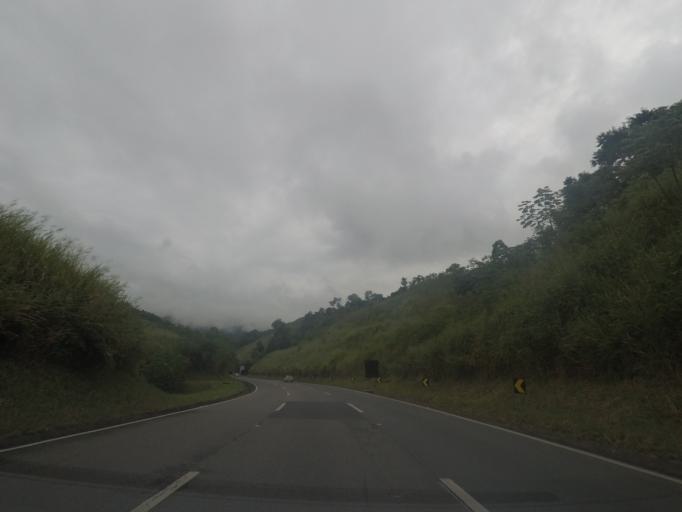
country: BR
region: Sao Paulo
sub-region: Cajati
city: Cajati
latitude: -24.8319
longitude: -48.2217
